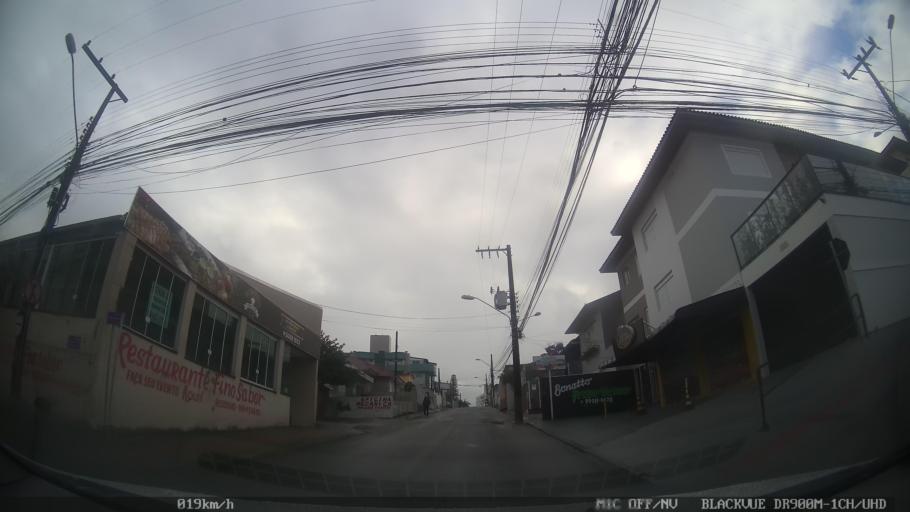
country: BR
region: Santa Catarina
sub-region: Sao Jose
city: Campinas
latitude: -27.5760
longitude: -48.6092
